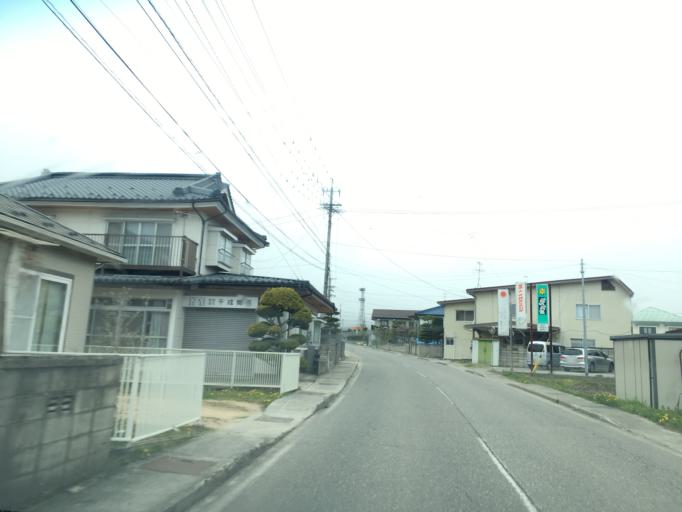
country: JP
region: Nagano
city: Omachi
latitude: 36.5110
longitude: 137.8480
